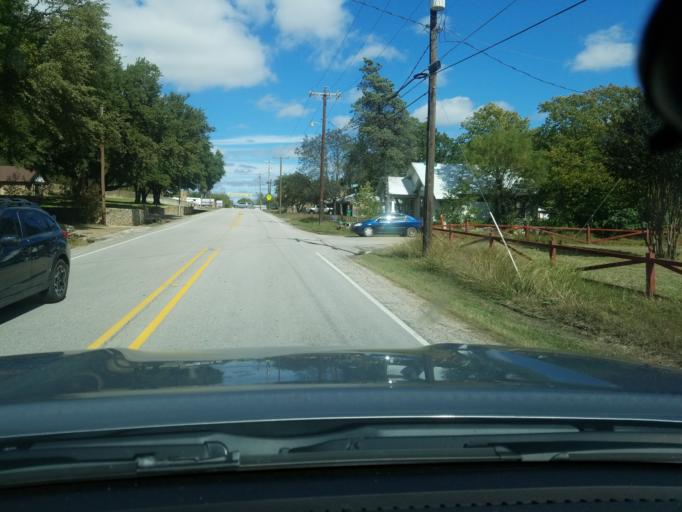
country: US
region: Texas
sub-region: Hamilton County
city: Hamilton
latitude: 31.6949
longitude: -98.1276
